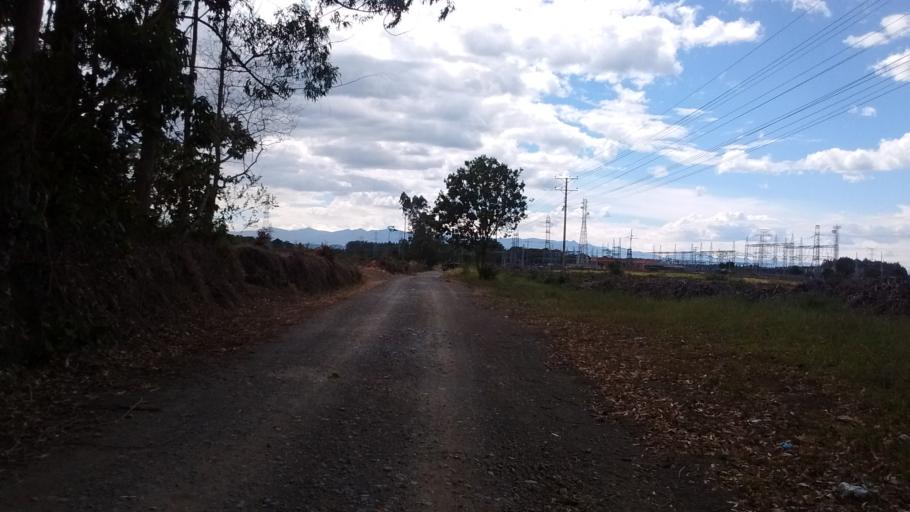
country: CO
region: Cauca
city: Popayan
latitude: 2.4962
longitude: -76.5916
